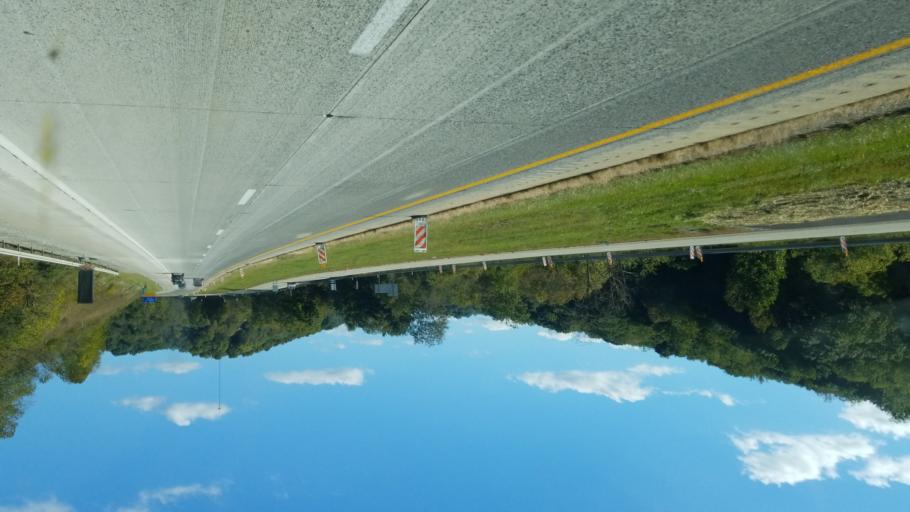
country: US
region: West Virginia
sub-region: Monongalia County
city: Star City
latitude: 39.7556
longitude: -80.0795
